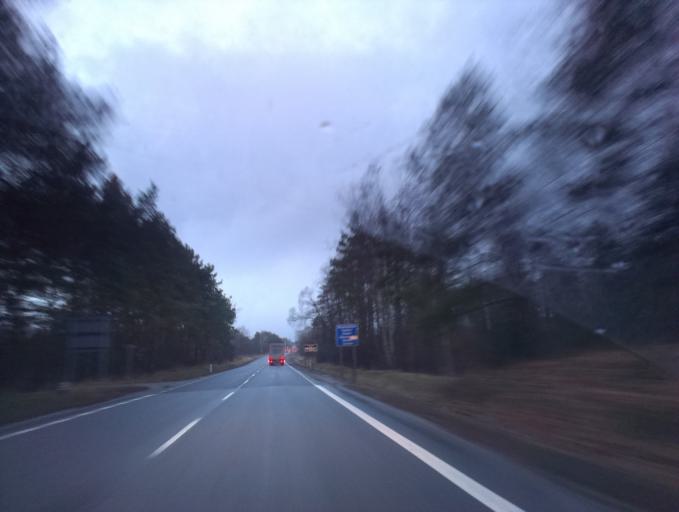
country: PL
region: Swietokrzyskie
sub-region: Powiat konecki
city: Ruda Maleniecka
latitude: 51.1992
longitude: 20.2062
